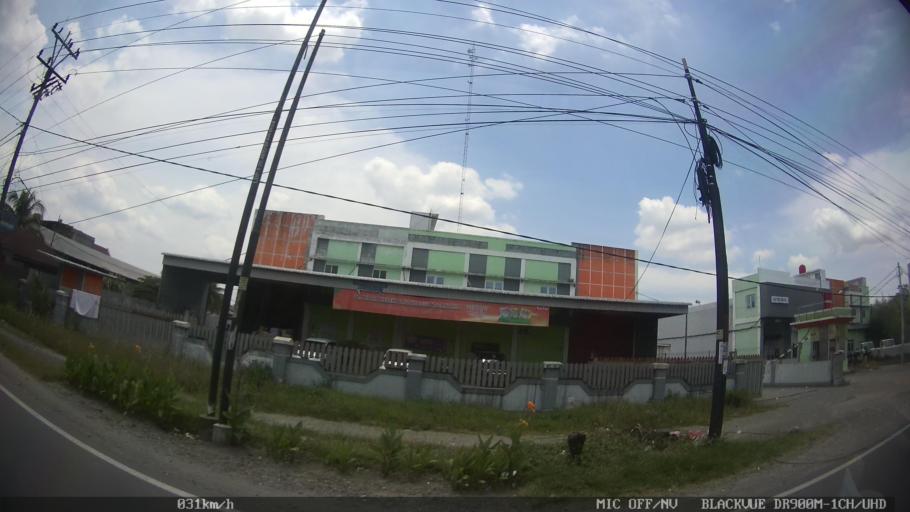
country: ID
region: North Sumatra
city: Binjai
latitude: 3.6012
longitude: 98.5464
